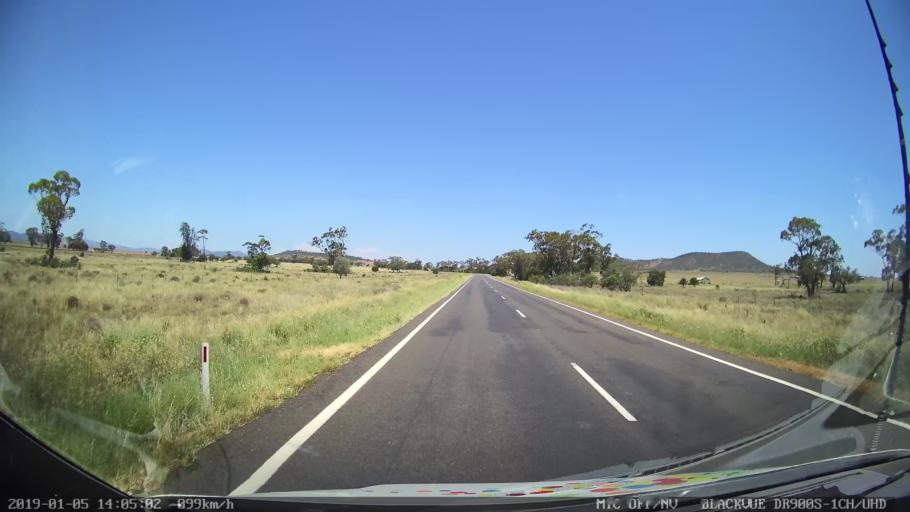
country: AU
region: New South Wales
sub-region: Gunnedah
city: Gunnedah
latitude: -31.2062
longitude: 150.3707
